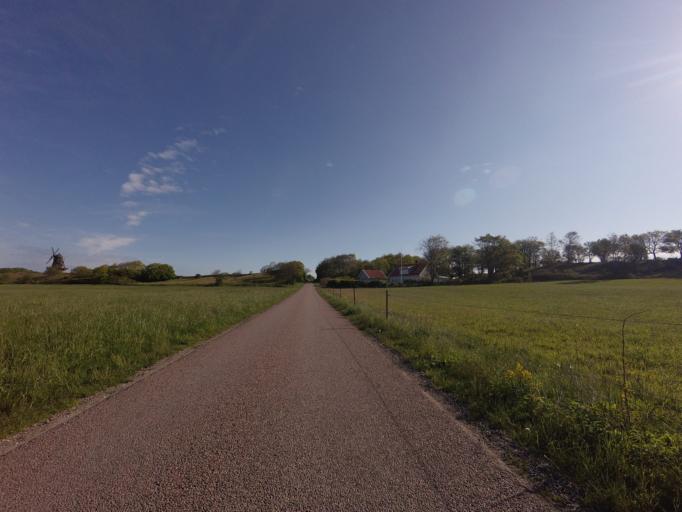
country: SE
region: Skane
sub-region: Hoganas Kommun
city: Hoganas
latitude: 56.2536
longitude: 12.5358
